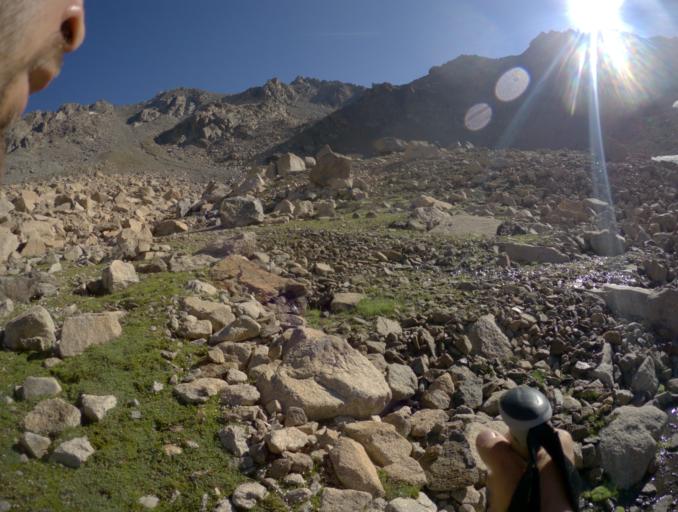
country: RU
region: Kabardino-Balkariya
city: Terskol
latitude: 43.3253
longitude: 42.5318
